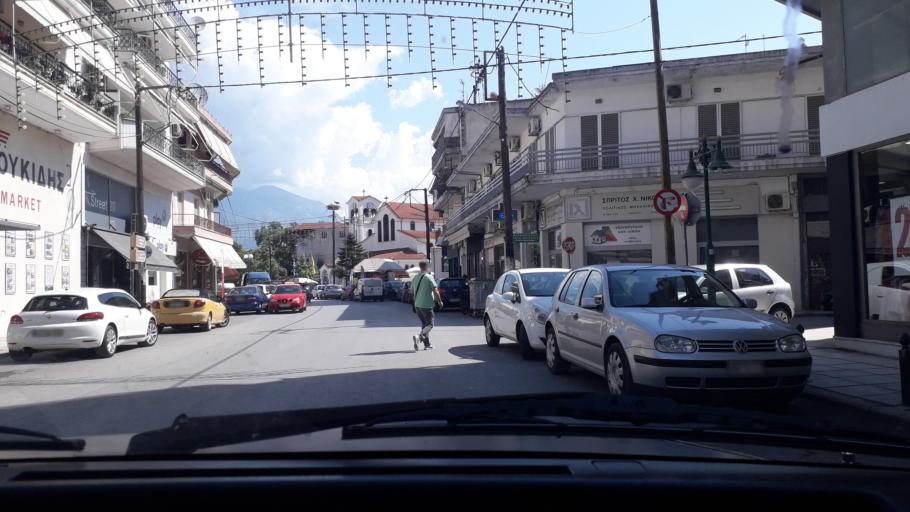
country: GR
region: Central Macedonia
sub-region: Nomos Pellis
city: Aridaia
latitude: 40.9738
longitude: 22.0604
